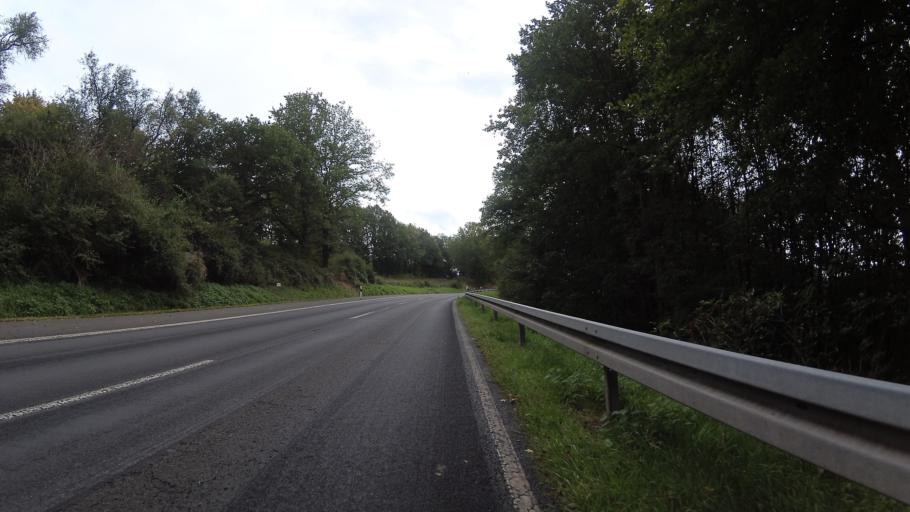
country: DE
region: Saarland
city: Namborn
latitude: 49.5072
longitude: 7.1619
